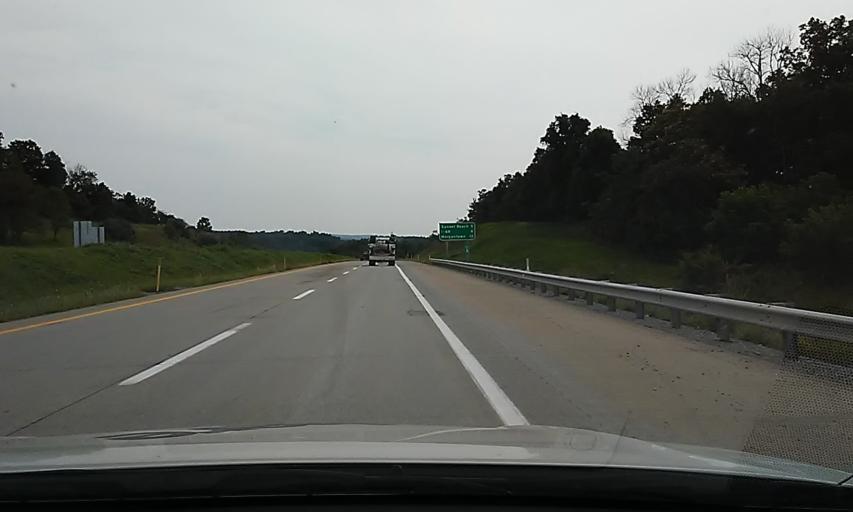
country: US
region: West Virginia
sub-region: Monongalia County
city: Cheat Lake
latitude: 39.7310
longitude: -79.8141
